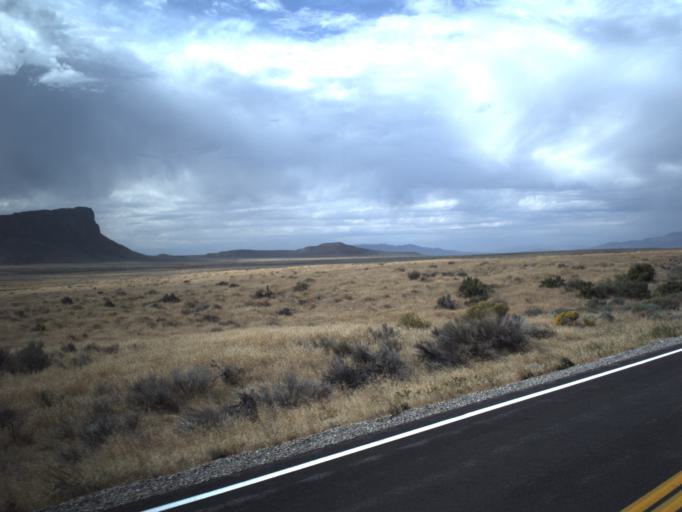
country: US
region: Utah
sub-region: Tooele County
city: Wendover
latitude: 41.3765
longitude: -114.0093
